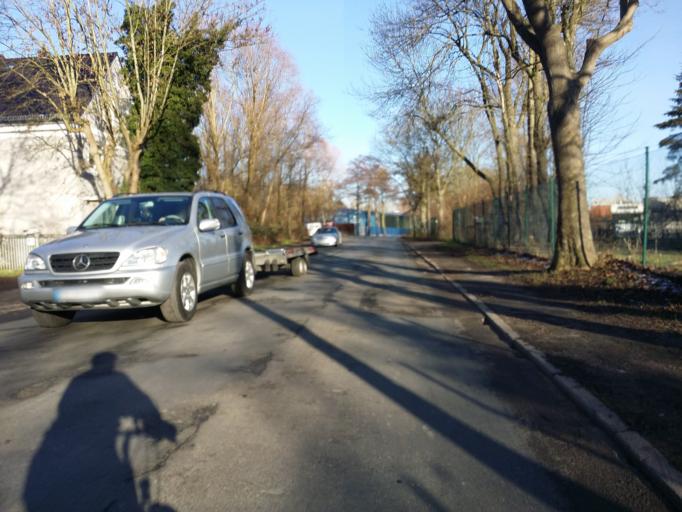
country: DE
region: Lower Saxony
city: Stuhr
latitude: 53.0695
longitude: 8.7615
